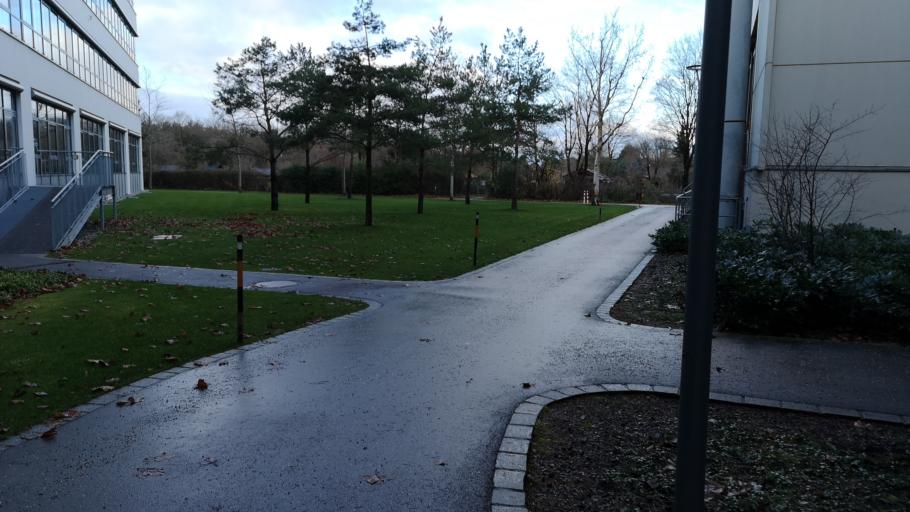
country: DE
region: Bavaria
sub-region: Upper Bavaria
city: Garching bei Munchen
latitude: 48.2526
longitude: 11.6331
